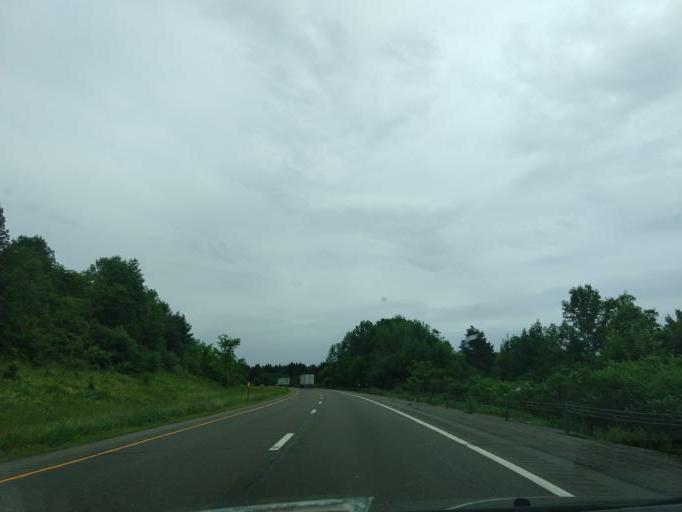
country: US
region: Pennsylvania
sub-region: Susquehanna County
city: Hallstead
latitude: 42.0207
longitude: -75.7838
